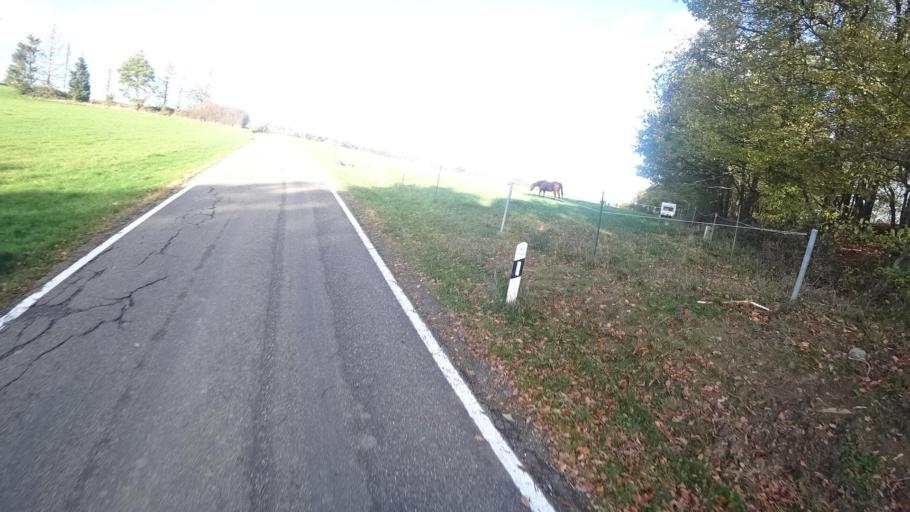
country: DE
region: Rheinland-Pfalz
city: Berg
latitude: 50.5242
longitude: 6.9503
